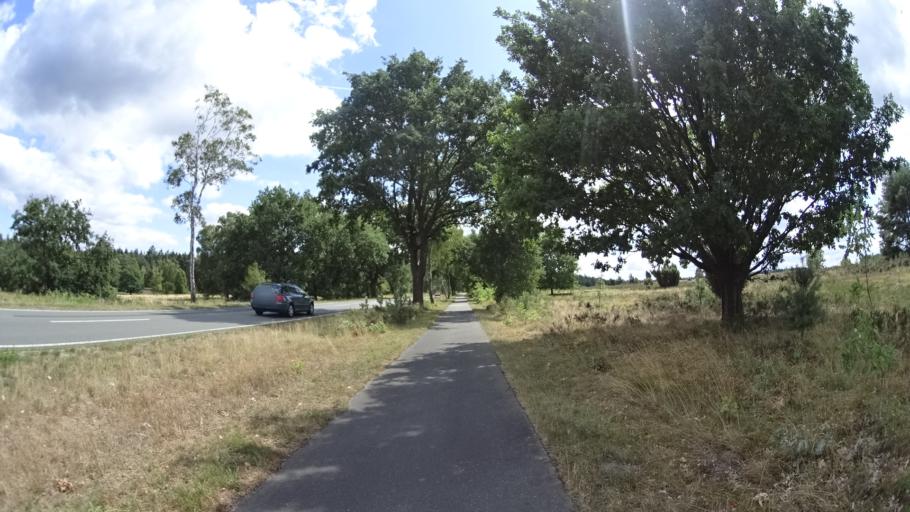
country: DE
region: Lower Saxony
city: Undeloh
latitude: 53.2145
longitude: 9.9485
